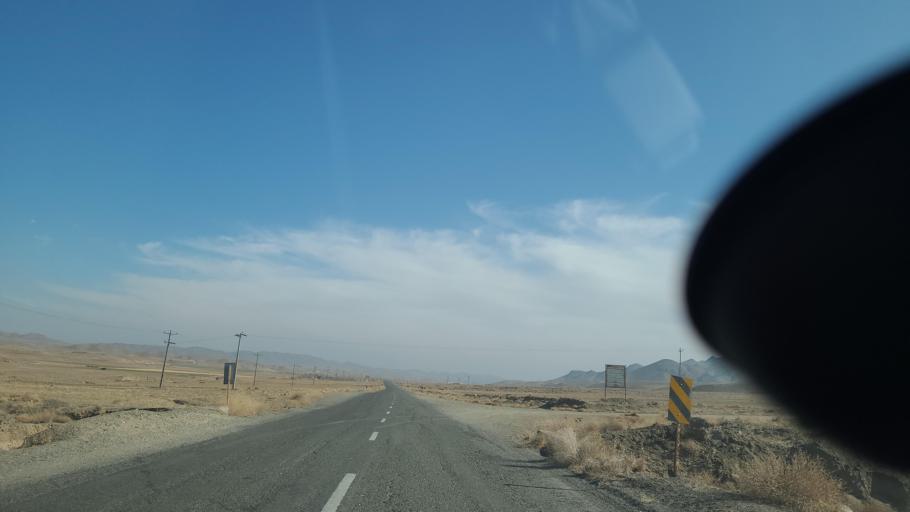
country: IR
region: Razavi Khorasan
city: Fariman
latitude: 35.5873
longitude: 59.6490
